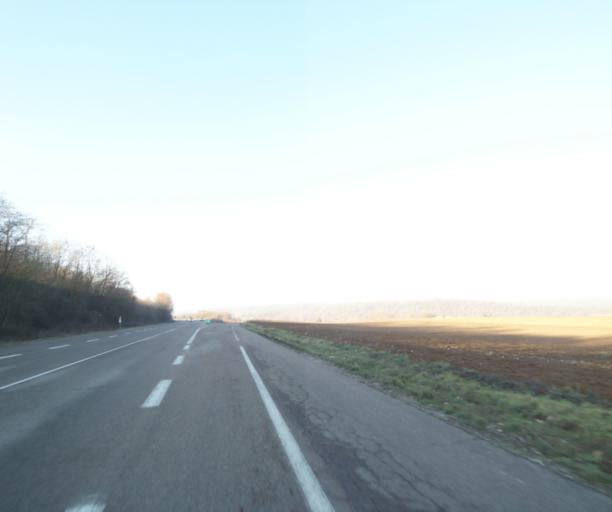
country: FR
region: Champagne-Ardenne
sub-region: Departement de la Haute-Marne
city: Chevillon
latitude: 48.5376
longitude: 5.0882
